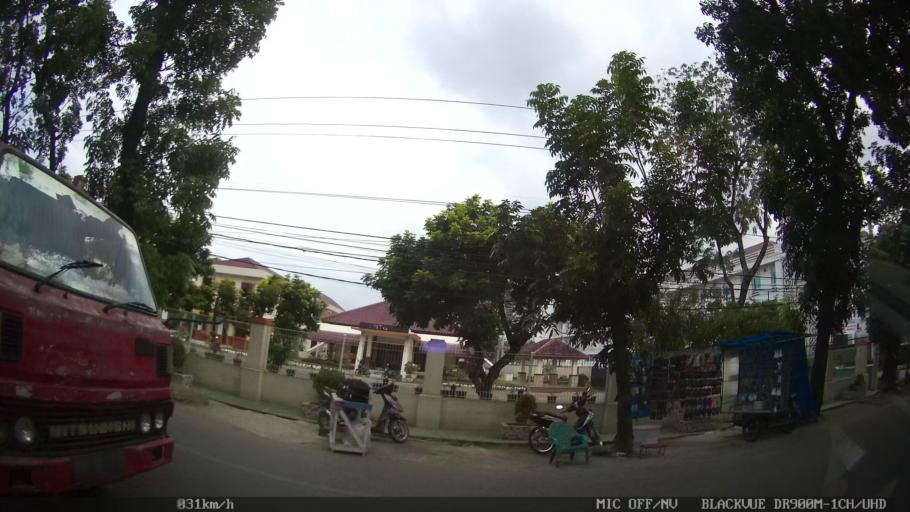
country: ID
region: North Sumatra
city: Deli Tua
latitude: 3.5415
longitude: 98.6773
